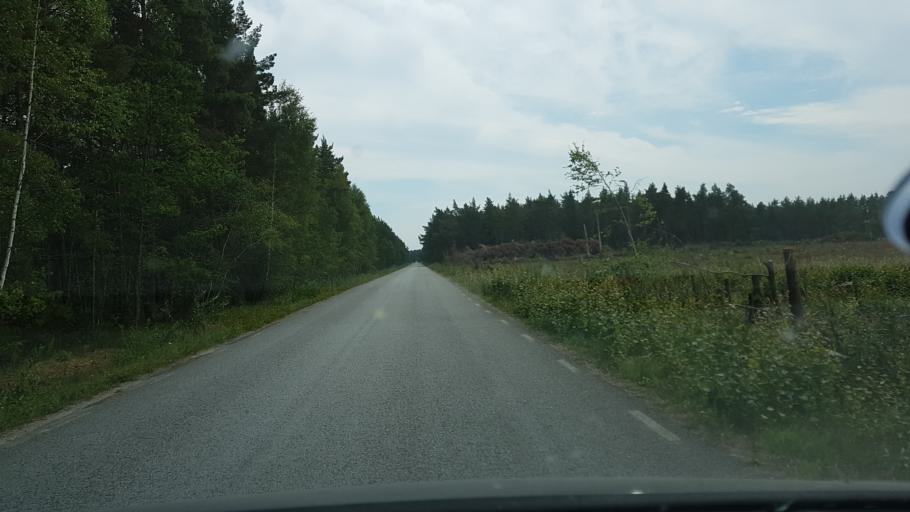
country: SE
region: Gotland
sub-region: Gotland
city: Visby
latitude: 57.7256
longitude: 18.5073
